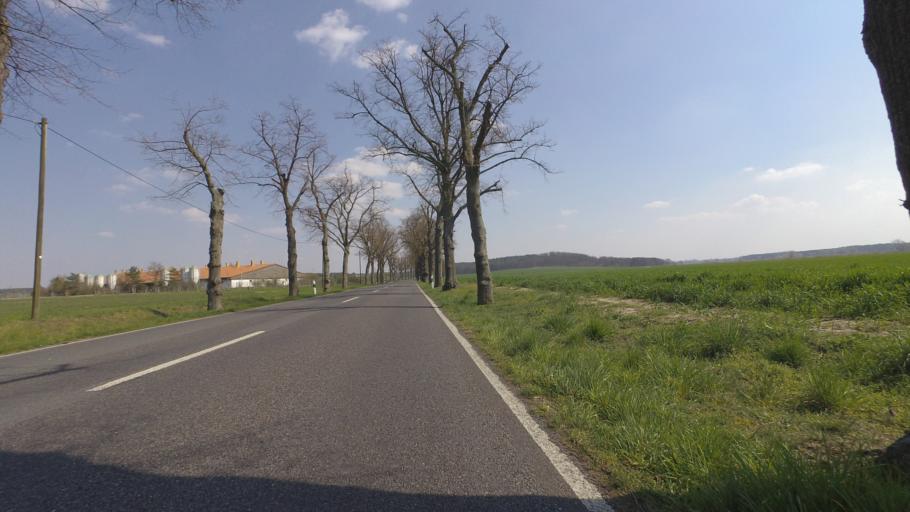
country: DE
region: Brandenburg
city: Mittenwalde
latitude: 52.2709
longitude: 13.4869
